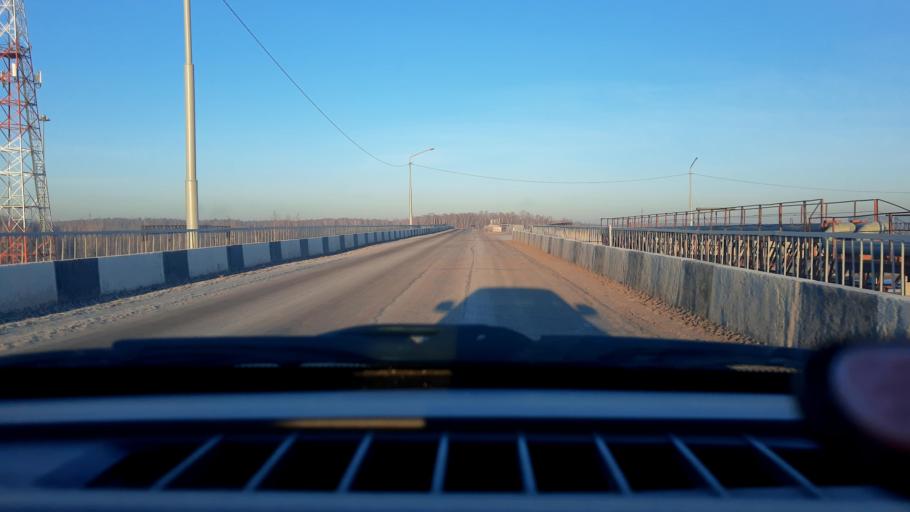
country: RU
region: Nizjnij Novgorod
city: Gorbatovka
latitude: 56.2805
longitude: 43.8426
